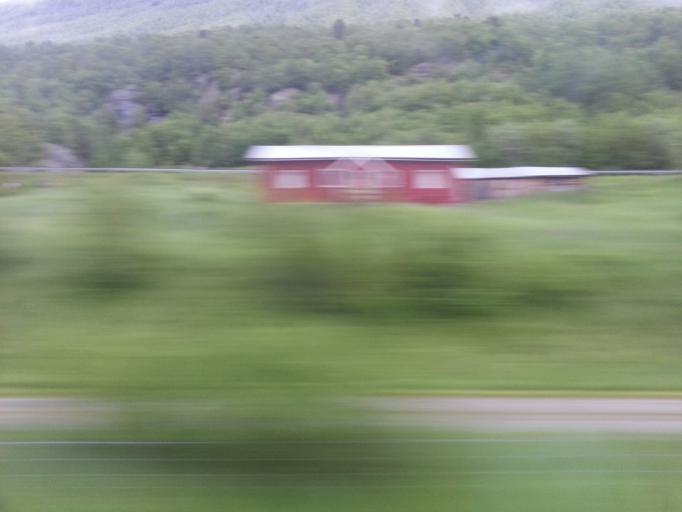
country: NO
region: Sor-Trondelag
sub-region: Oppdal
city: Oppdal
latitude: 62.4921
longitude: 9.5865
